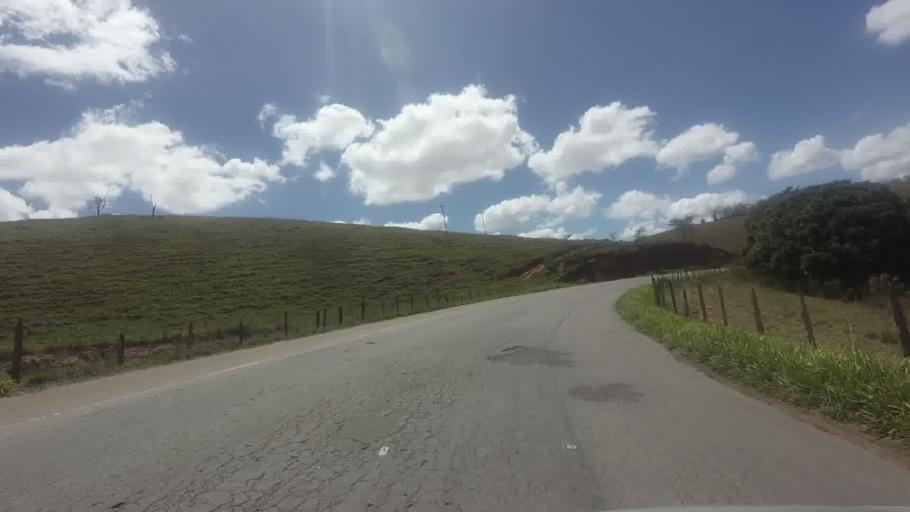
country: BR
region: Rio de Janeiro
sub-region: Santo Antonio De Padua
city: Santo Antonio de Padua
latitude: -21.6548
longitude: -42.3172
